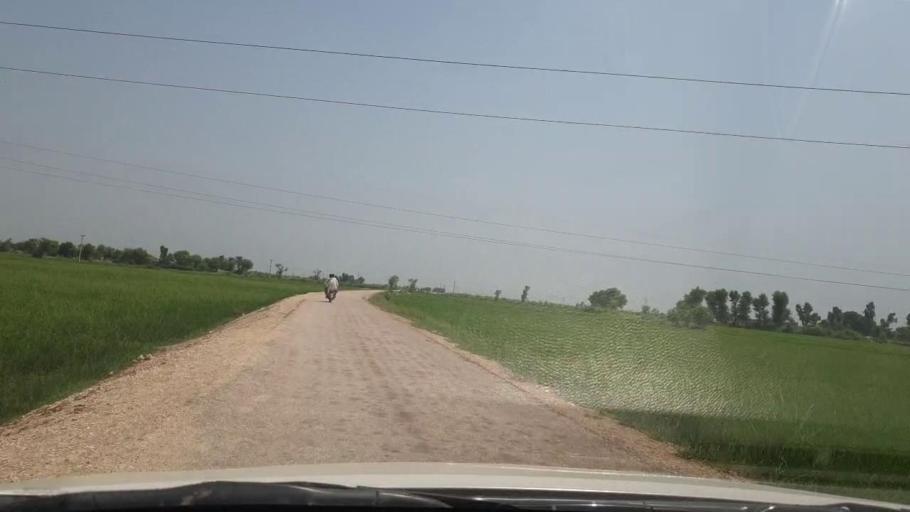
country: PK
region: Sindh
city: Rustam jo Goth
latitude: 28.0228
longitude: 68.8002
